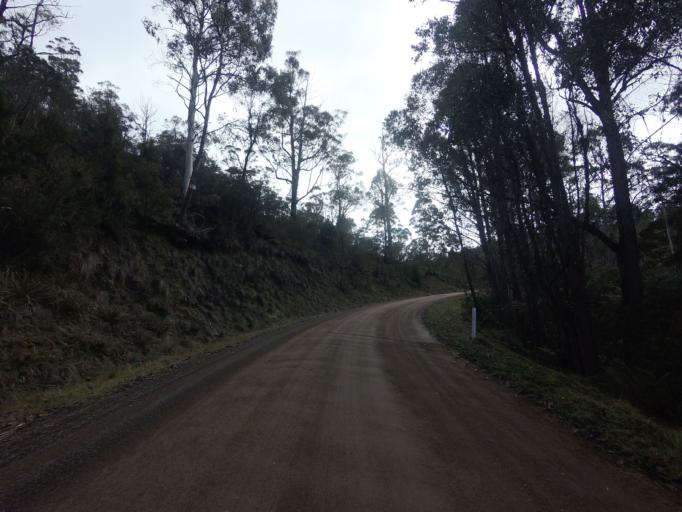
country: AU
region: Tasmania
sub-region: Derwent Valley
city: New Norfolk
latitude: -42.7510
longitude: 146.8698
